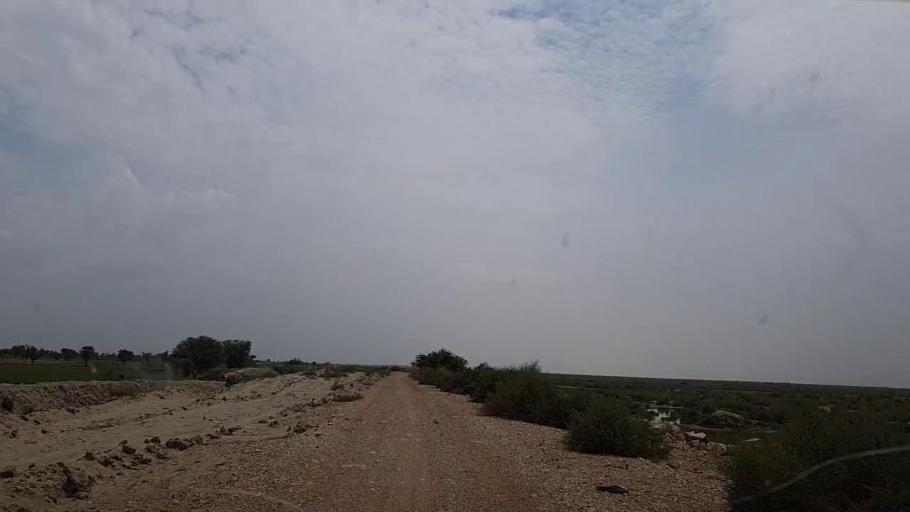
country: PK
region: Sindh
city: Phulji
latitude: 26.8457
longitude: 67.6190
